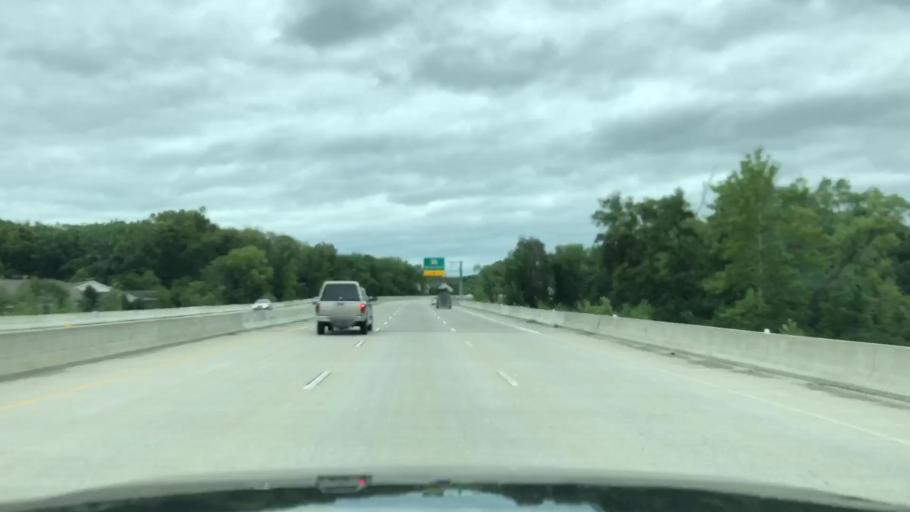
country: US
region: Missouri
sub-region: Saint Louis County
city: Maryland Heights
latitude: 38.6911
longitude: -90.4980
